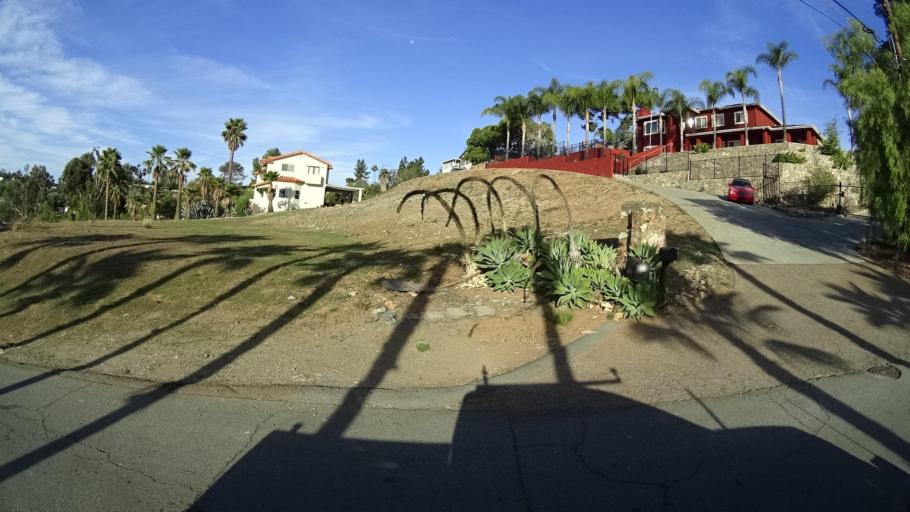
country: US
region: California
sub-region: San Diego County
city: Spring Valley
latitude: 32.7343
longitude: -116.9871
